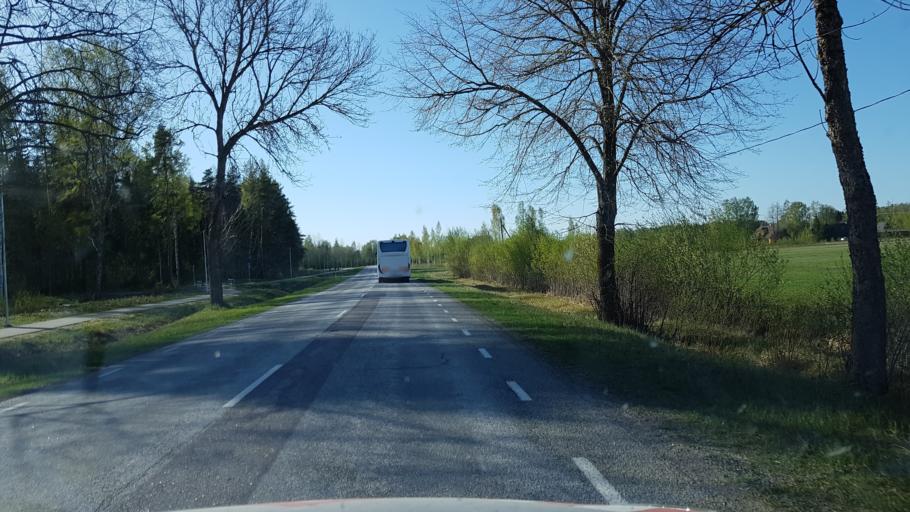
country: EE
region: Paernumaa
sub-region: Paikuse vald
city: Paikuse
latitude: 58.3640
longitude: 24.6462
